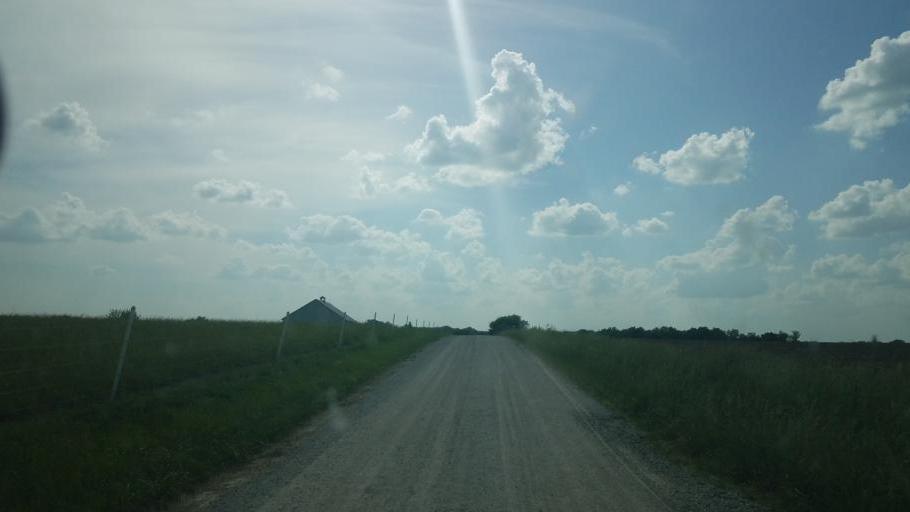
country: US
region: Missouri
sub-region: Cooper County
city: Boonville
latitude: 38.8502
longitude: -92.6337
